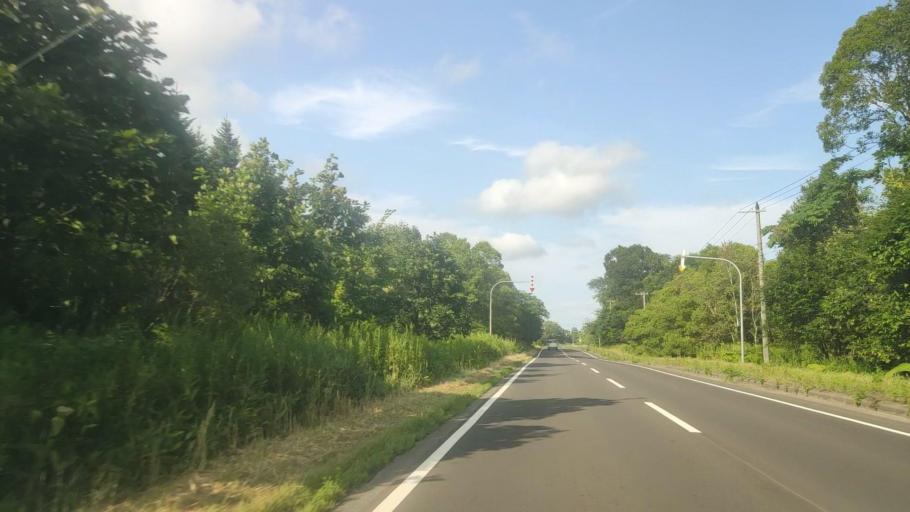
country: JP
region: Hokkaido
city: Chitose
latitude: 42.7368
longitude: 141.7792
